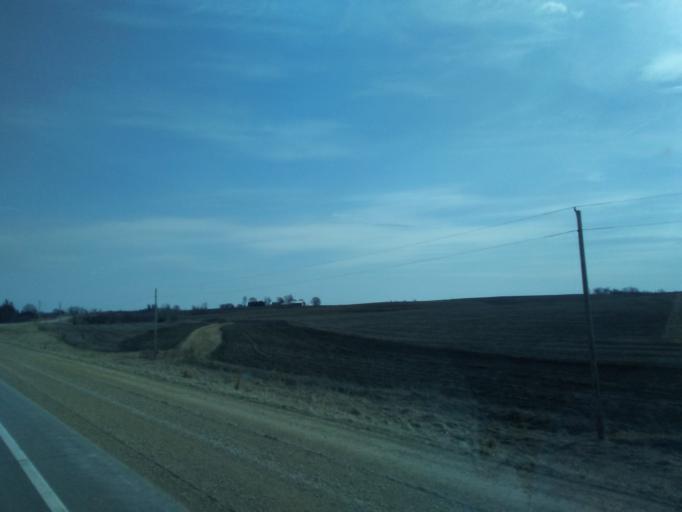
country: US
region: Iowa
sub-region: Winneshiek County
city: Decorah
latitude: 43.3961
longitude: -91.8375
